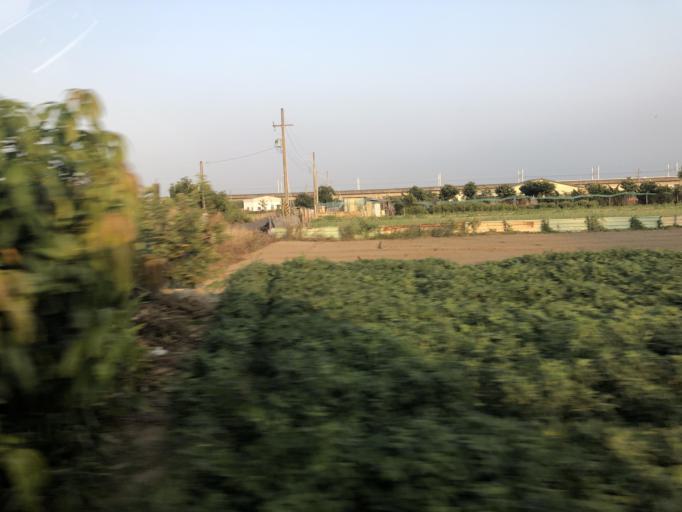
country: TW
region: Taiwan
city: Xinying
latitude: 23.1488
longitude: 120.2732
